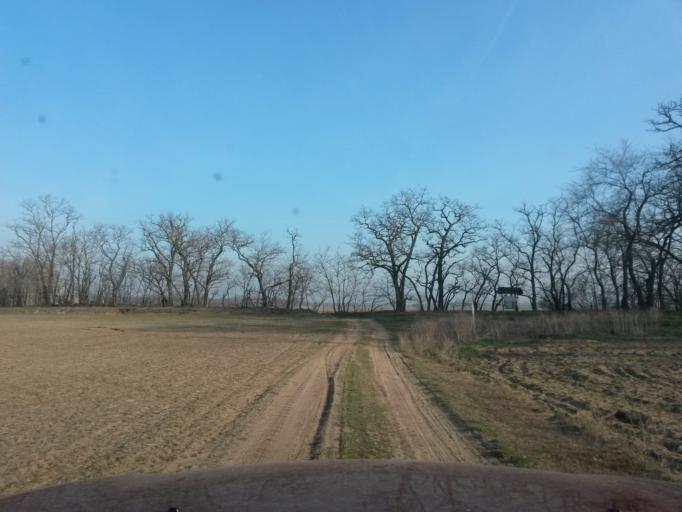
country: SK
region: Nitriansky
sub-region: Okres Komarno
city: Hurbanovo
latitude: 47.8876
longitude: 18.1709
